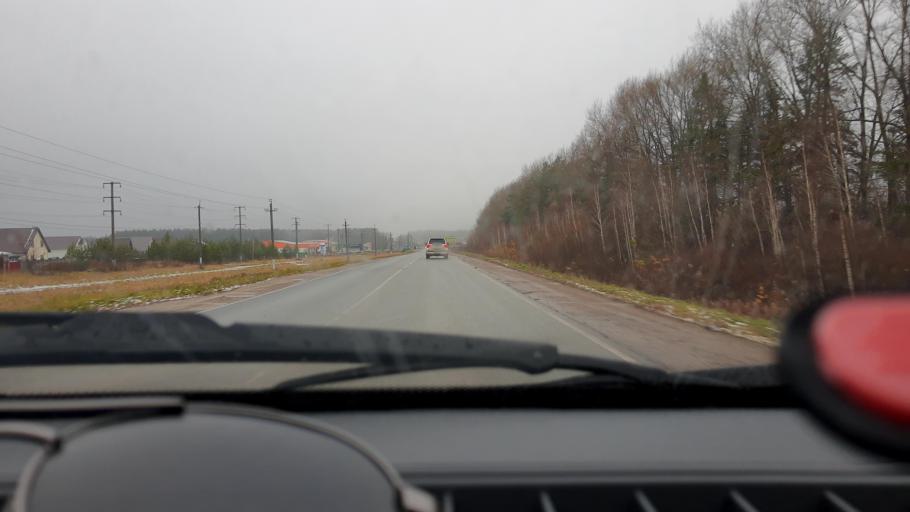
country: RU
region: Bashkortostan
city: Kabakovo
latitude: 54.6094
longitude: 56.1757
